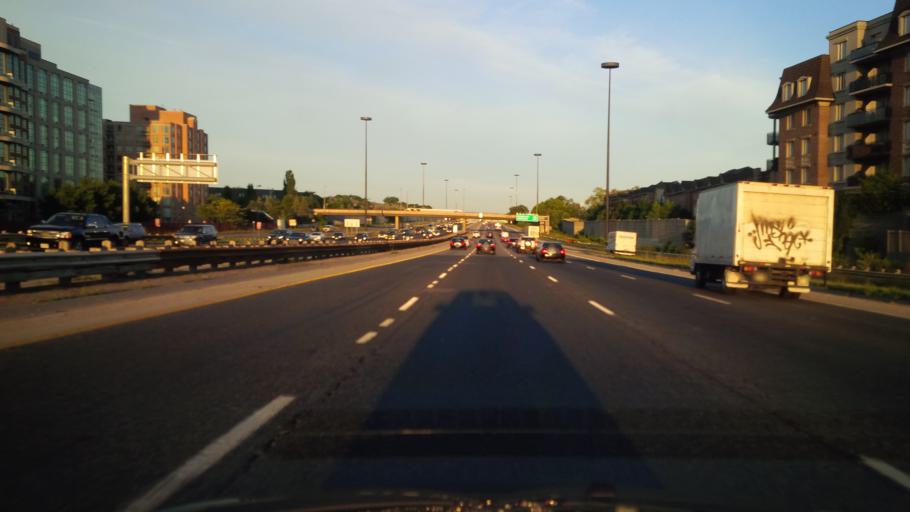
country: CA
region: Ontario
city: Etobicoke
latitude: 43.6257
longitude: -79.4899
